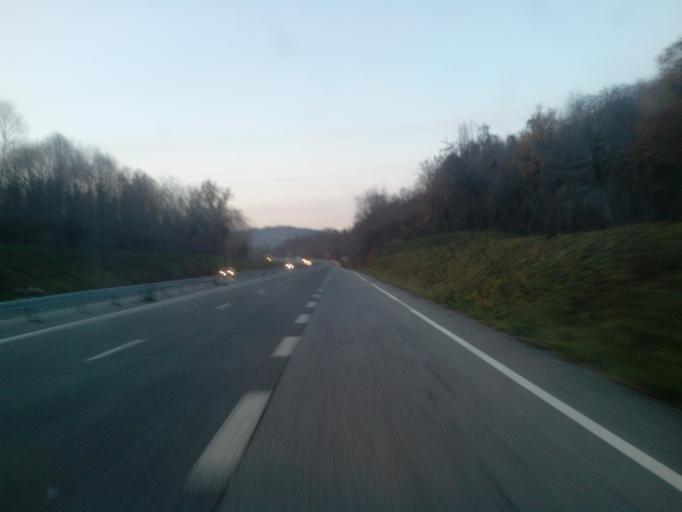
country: FR
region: Midi-Pyrenees
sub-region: Departement de l'Ariege
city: Montgaillard
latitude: 42.9244
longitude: 1.6348
